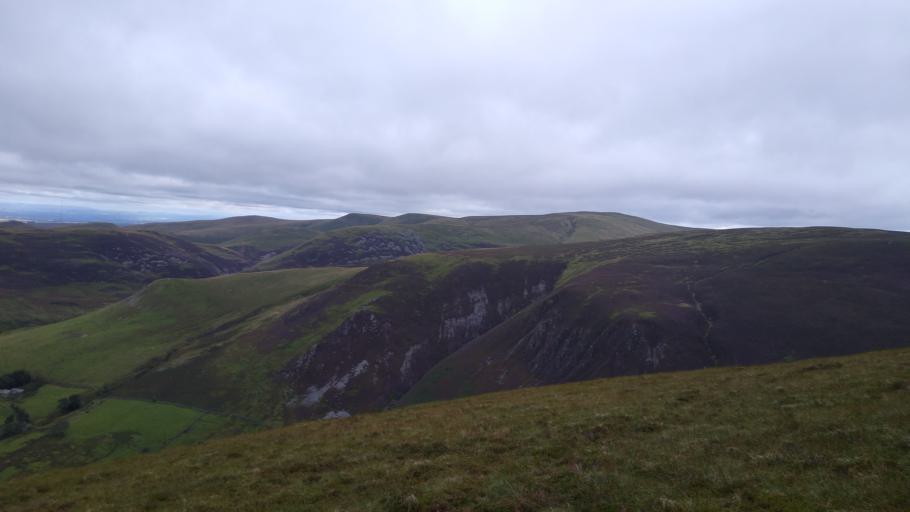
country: GB
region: England
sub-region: Cumbria
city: Keswick
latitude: 54.6693
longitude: -3.1402
